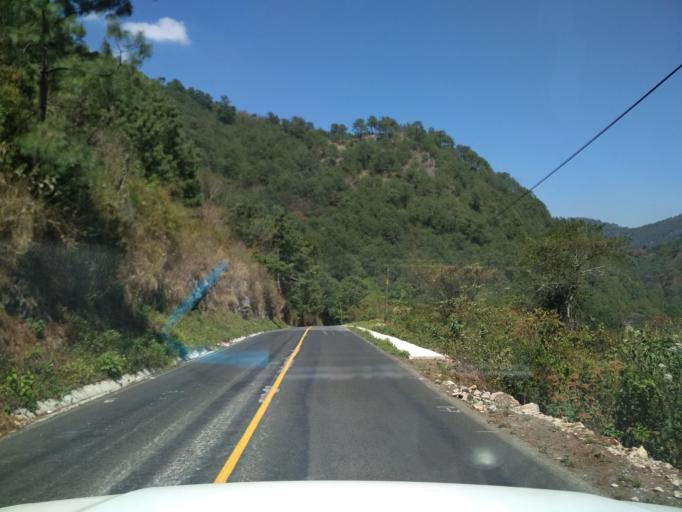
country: MX
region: Veracruz
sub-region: Tlilapan
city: Tonalixco
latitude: 18.7660
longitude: -97.0806
